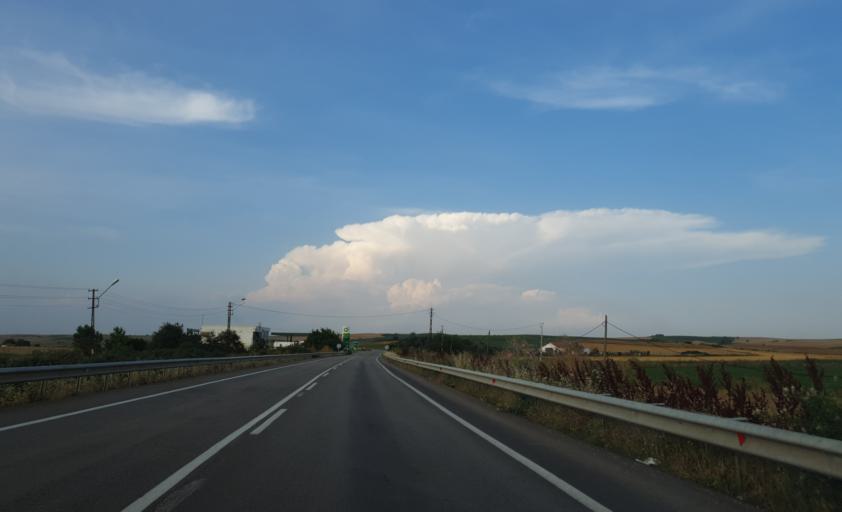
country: TR
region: Tekirdag
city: Hayrabolu
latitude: 41.2335
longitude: 27.1253
